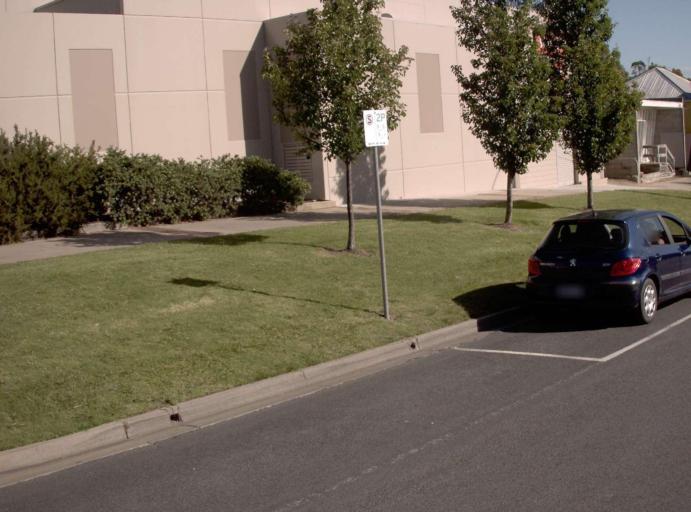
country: AU
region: Victoria
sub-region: East Gippsland
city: Lakes Entrance
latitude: -37.7078
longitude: 148.4546
